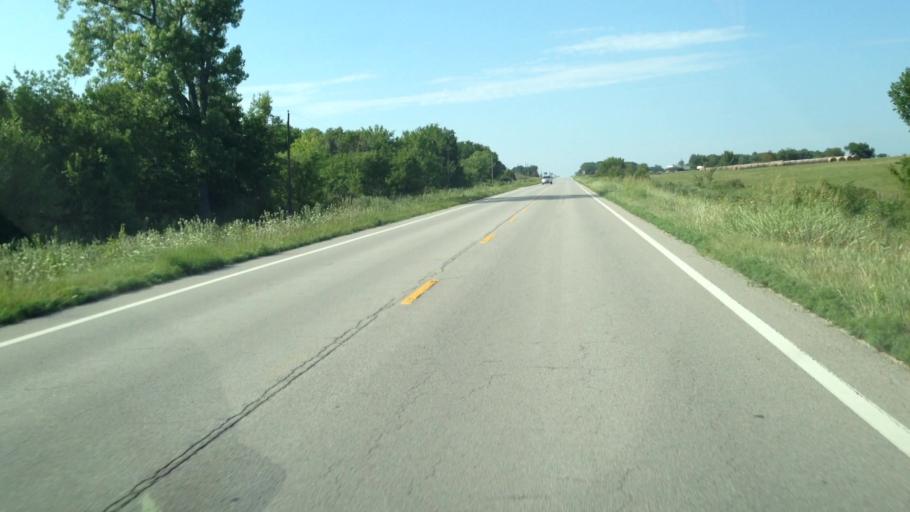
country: US
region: Kansas
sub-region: Neosho County
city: Erie
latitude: 37.7141
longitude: -95.1607
